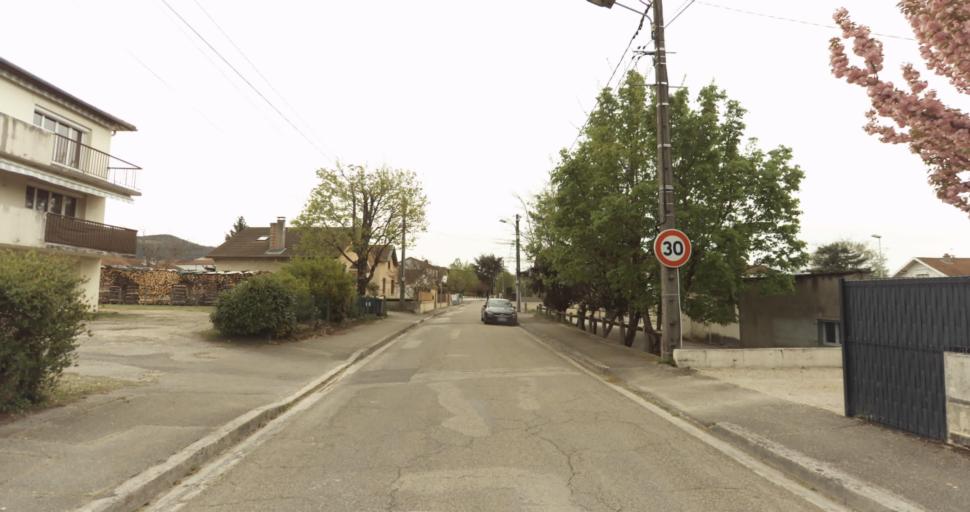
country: FR
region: Rhone-Alpes
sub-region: Departement de l'Ain
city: Amberieu-en-Bugey
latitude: 45.9659
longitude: 5.3517
